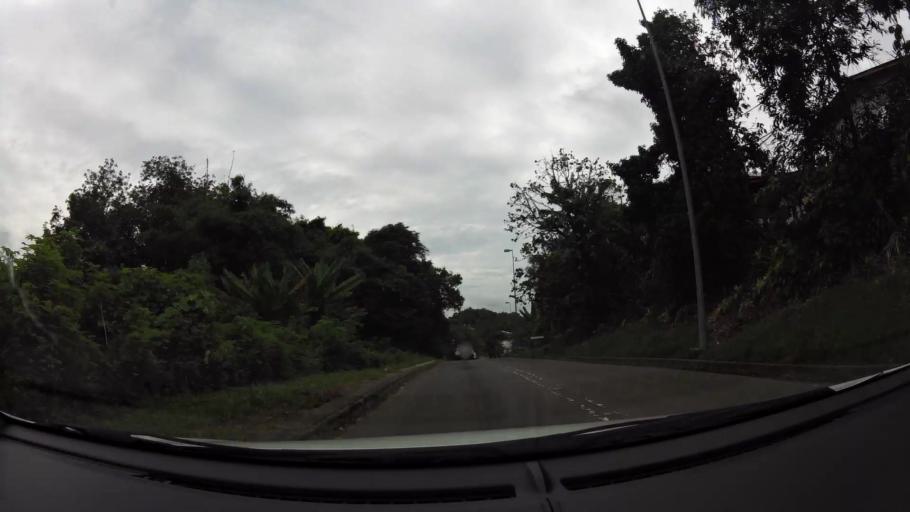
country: BN
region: Brunei and Muara
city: Bandar Seri Begawan
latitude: 4.8945
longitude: 114.9181
